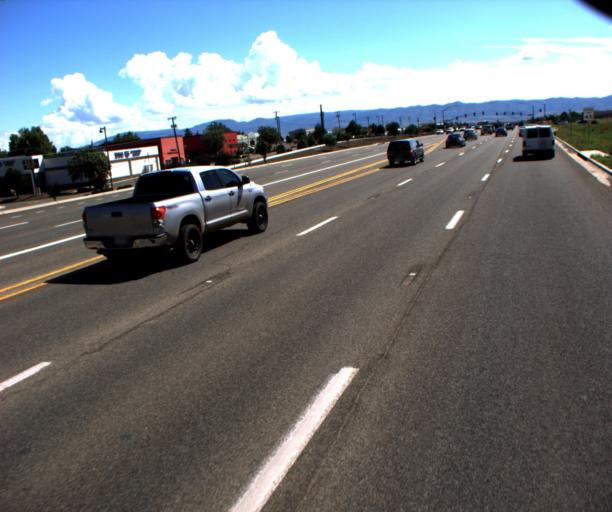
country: US
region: Arizona
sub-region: Yavapai County
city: Prescott Valley
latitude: 34.5798
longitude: -112.3592
